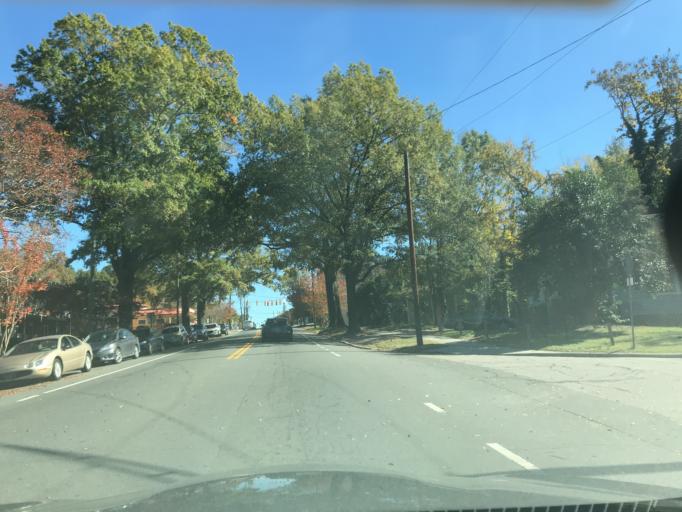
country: US
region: North Carolina
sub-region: Durham County
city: Durham
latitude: 35.9967
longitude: -78.9195
